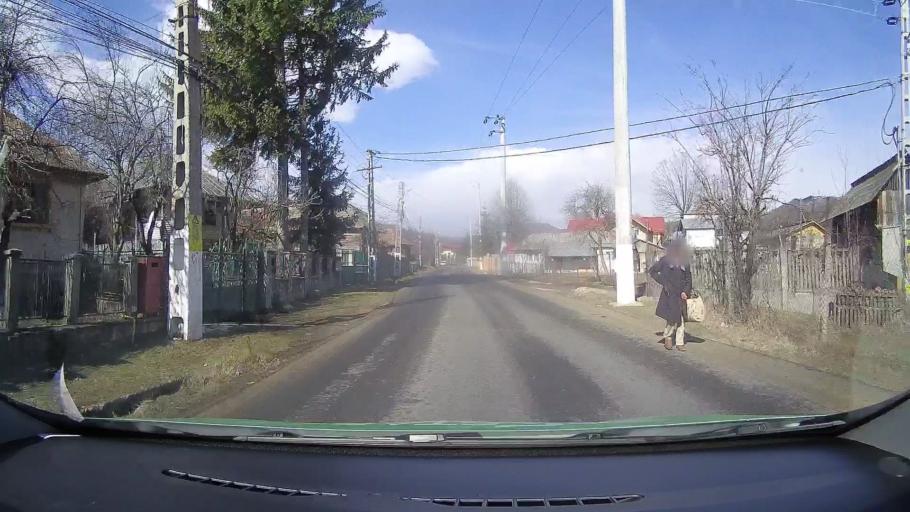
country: RO
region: Dambovita
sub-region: Comuna Runcu
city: Runcu
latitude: 45.1707
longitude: 25.3941
